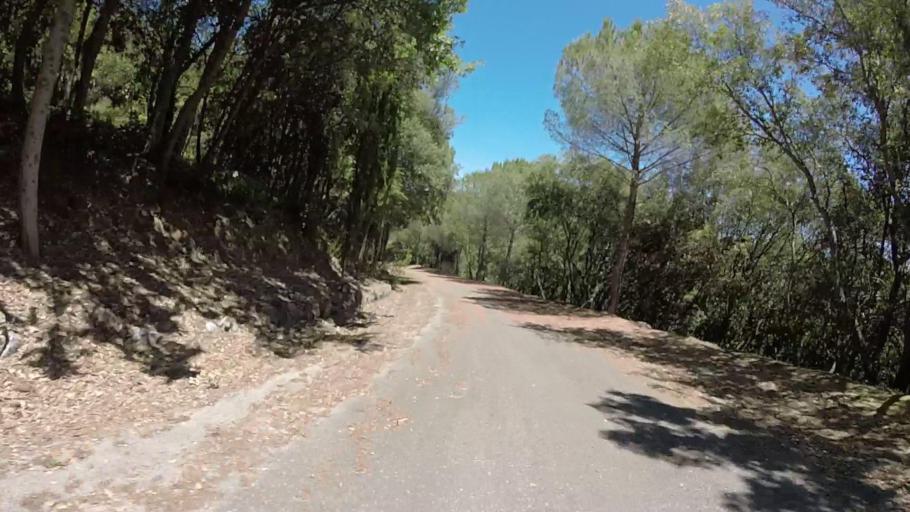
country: FR
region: Provence-Alpes-Cote d'Azur
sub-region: Departement des Alpes-Maritimes
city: Biot
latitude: 43.6274
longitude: 7.0640
